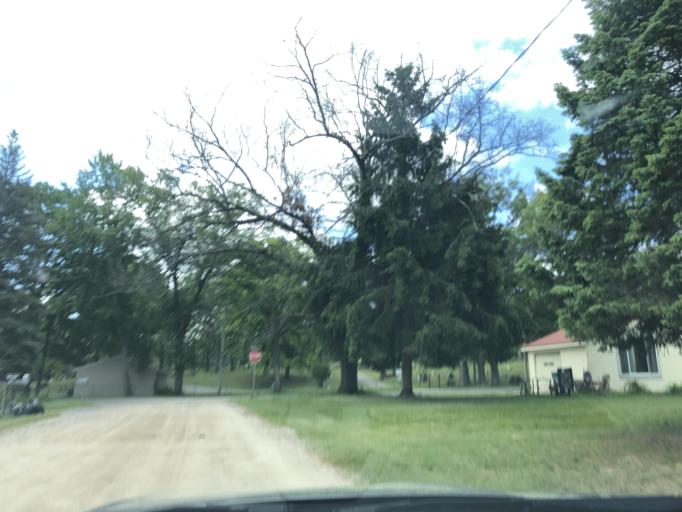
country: US
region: Michigan
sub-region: Clare County
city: Harrison
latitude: 44.0319
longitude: -84.8106
